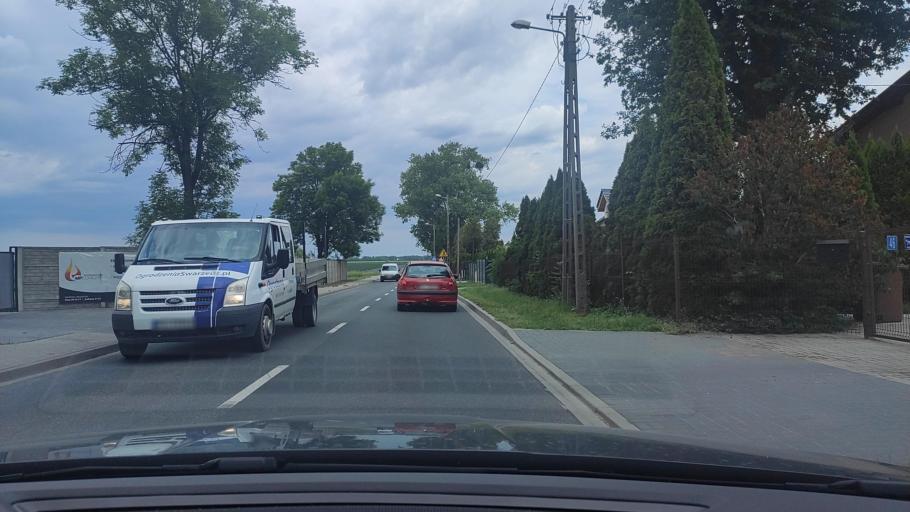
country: PL
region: Greater Poland Voivodeship
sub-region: Powiat poznanski
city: Swarzedz
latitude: 52.4259
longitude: 17.1579
